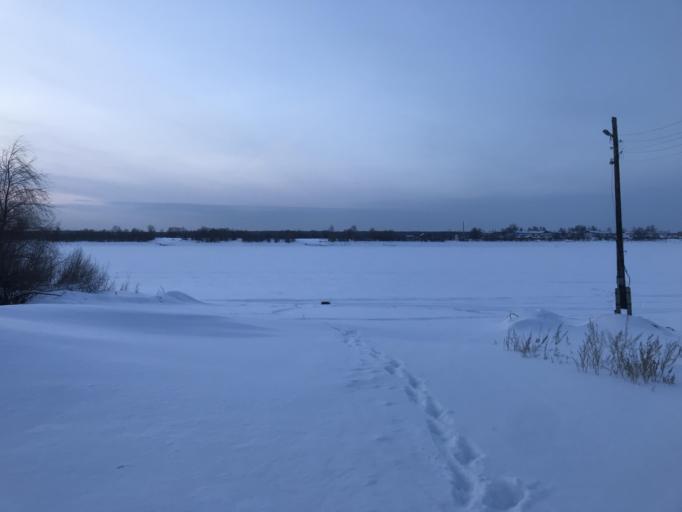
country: RU
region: Tjumen
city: Tobol'sk
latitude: 58.1944
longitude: 68.2320
